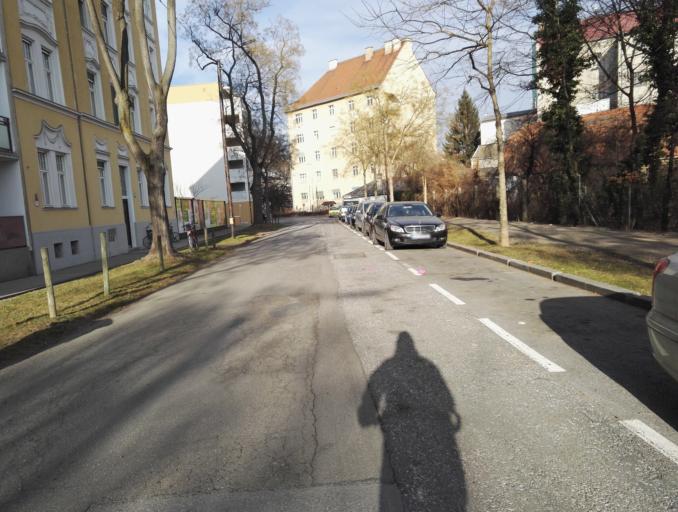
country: AT
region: Styria
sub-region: Graz Stadt
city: Graz
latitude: 47.0646
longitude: 15.4272
